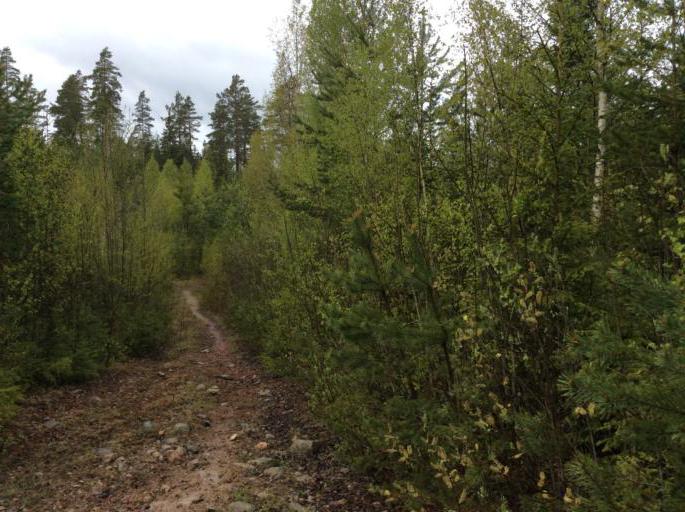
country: SE
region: Dalarna
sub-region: Avesta Kommun
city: Avesta
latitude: 60.1897
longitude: 16.1844
